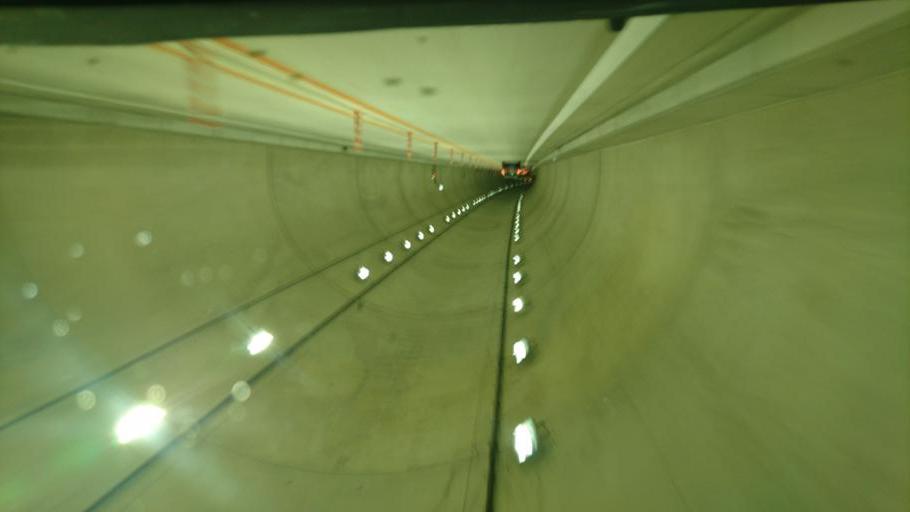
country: JP
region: Iwate
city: Kamaishi
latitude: 39.2677
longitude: 141.8464
